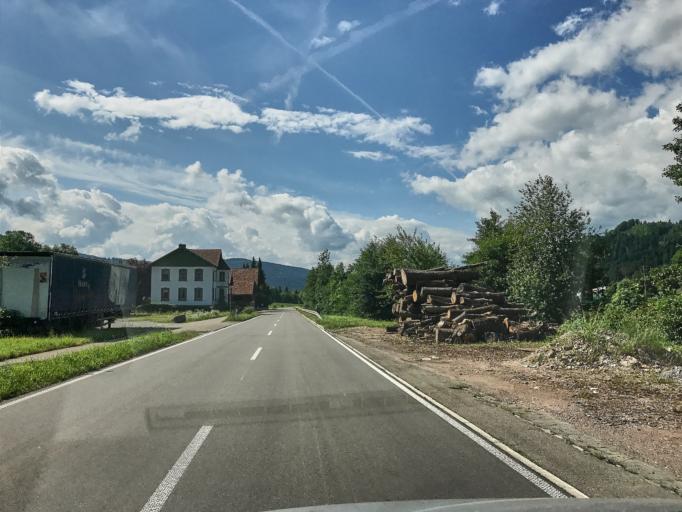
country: DE
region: Baden-Wuerttemberg
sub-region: Freiburg Region
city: Biberach
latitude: 48.3560
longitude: 8.0615
